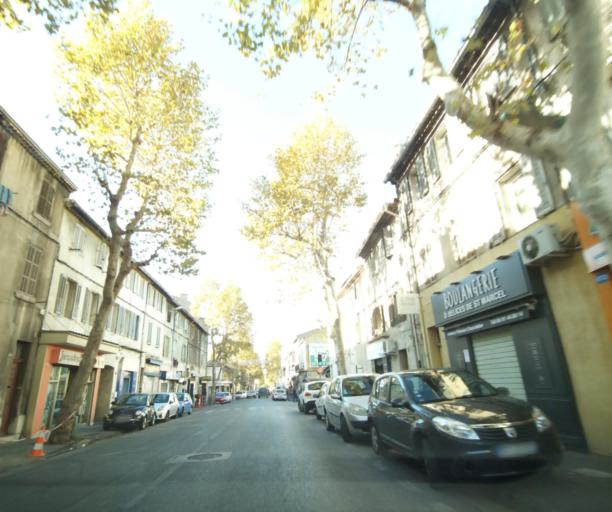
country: FR
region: Provence-Alpes-Cote d'Azur
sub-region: Departement des Bouches-du-Rhone
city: Marseille 11
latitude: 43.2874
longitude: 5.4656
